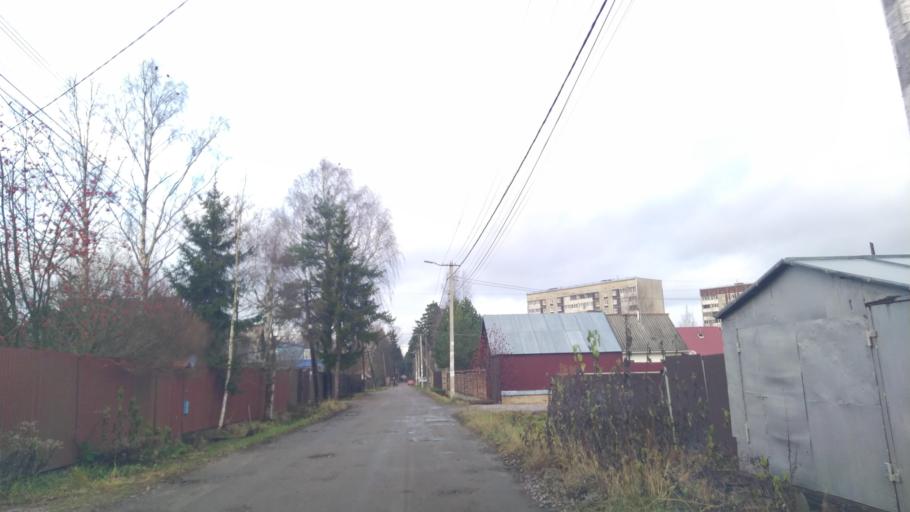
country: RU
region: Leningrad
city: Vsevolozhsk
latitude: 60.0210
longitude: 30.6236
